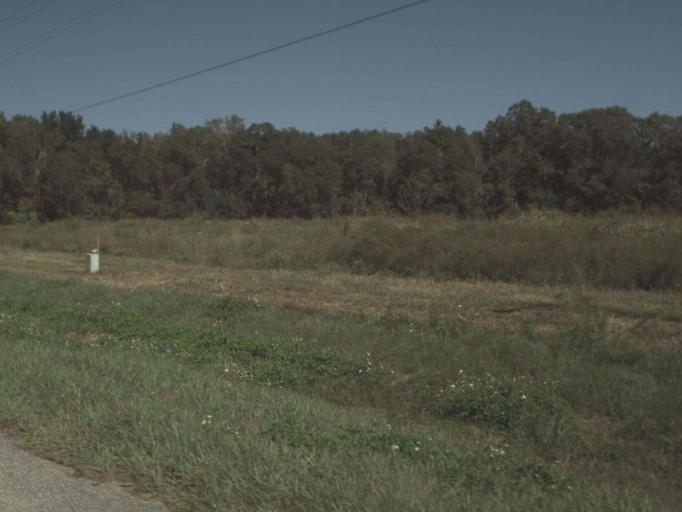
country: US
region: Florida
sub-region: Jefferson County
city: Monticello
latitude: 30.3813
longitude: -84.0060
